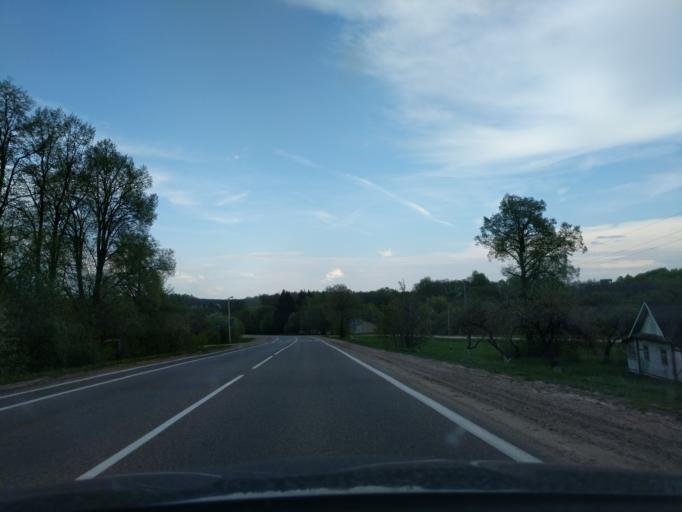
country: BY
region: Grodnenskaya
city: Navahrudak
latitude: 53.6170
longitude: 25.8730
